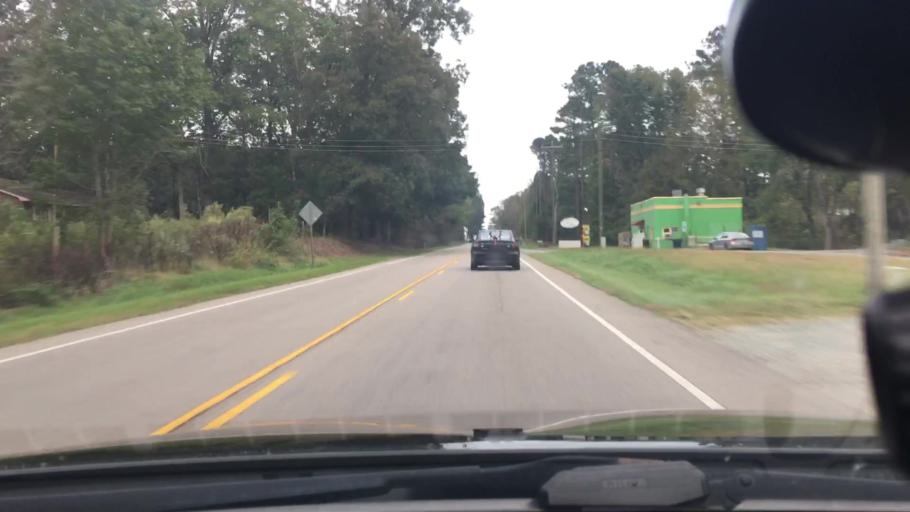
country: US
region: North Carolina
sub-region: Moore County
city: Robbins
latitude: 35.4024
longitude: -79.5582
